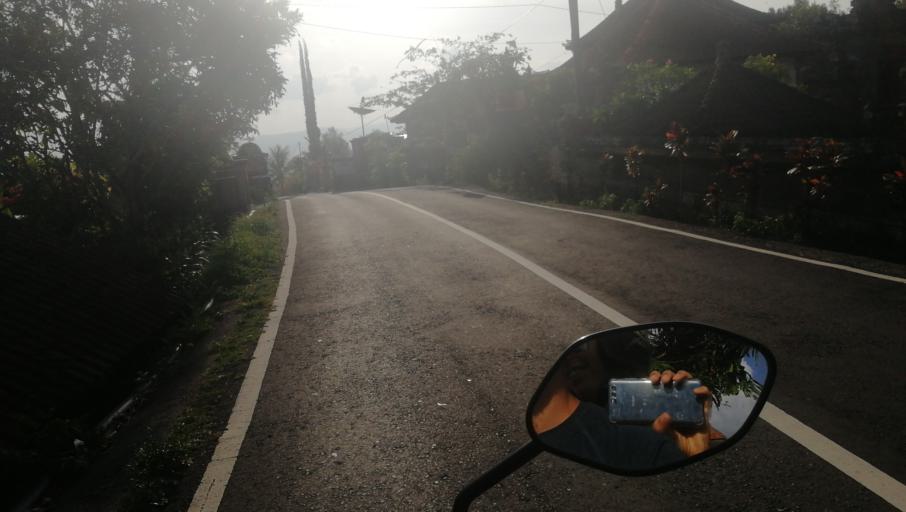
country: ID
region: Bali
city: Munduk
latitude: -8.2653
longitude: 115.0587
